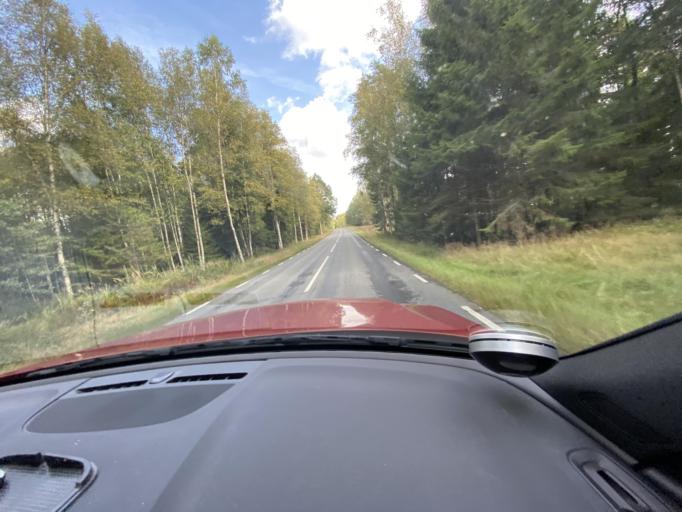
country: SE
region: Skane
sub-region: Hassleholms Kommun
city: Bjarnum
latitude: 56.3547
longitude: 13.7601
